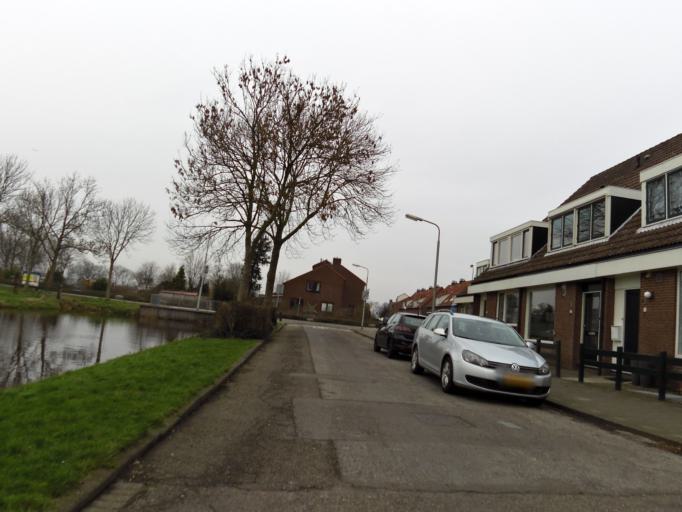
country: NL
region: South Holland
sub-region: Gemeente Leiderdorp
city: Leiderdorp
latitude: 52.1922
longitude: 4.5785
